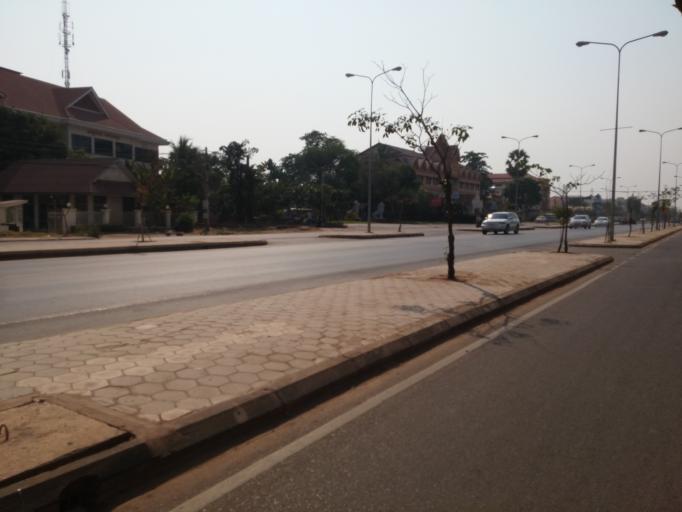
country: KH
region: Siem Reap
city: Siem Reap
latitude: 13.3683
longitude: 103.8479
